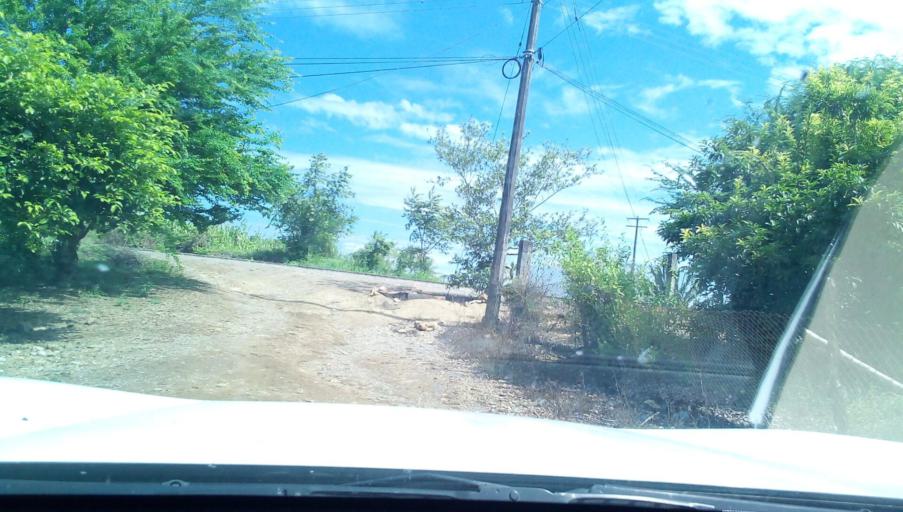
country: MX
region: Veracruz
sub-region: Alamo Temapache
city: Vegas de la Soledad y Soledad Dos
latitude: 20.8974
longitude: -97.9451
